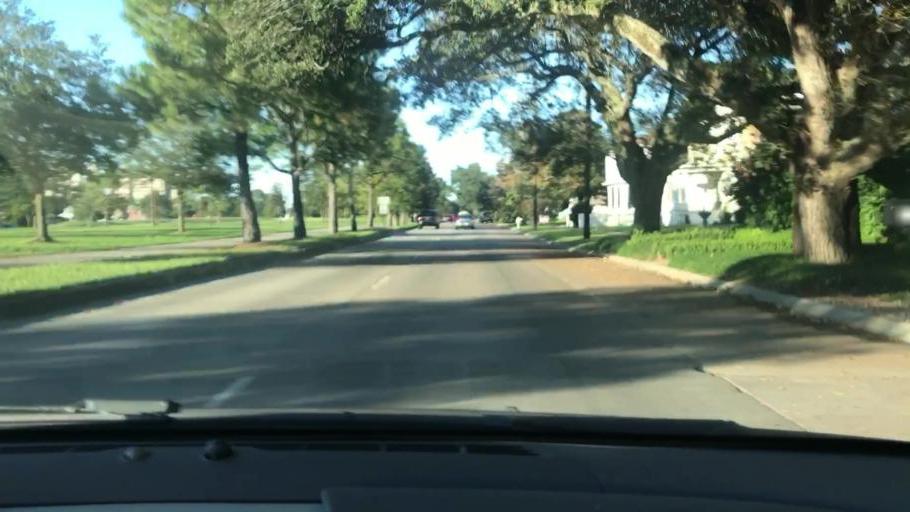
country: US
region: Louisiana
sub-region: Jefferson Parish
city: Metairie
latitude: 30.0133
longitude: -90.1140
